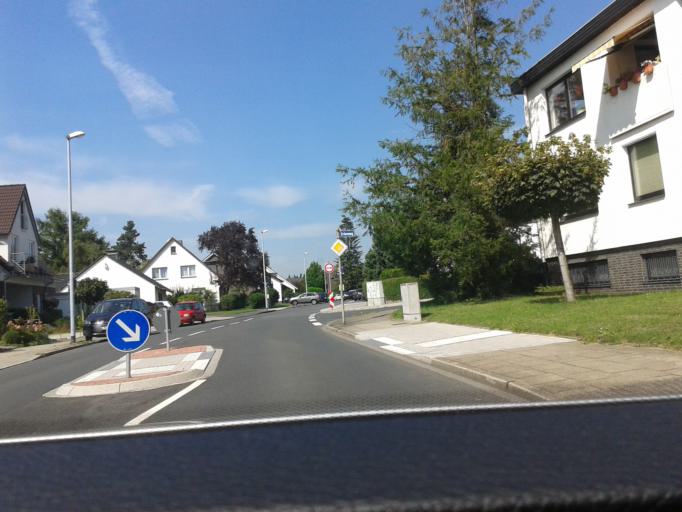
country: DE
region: North Rhine-Westphalia
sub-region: Regierungsbezirk Dusseldorf
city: Muelheim (Ruhr)
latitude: 51.3926
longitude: 6.8587
